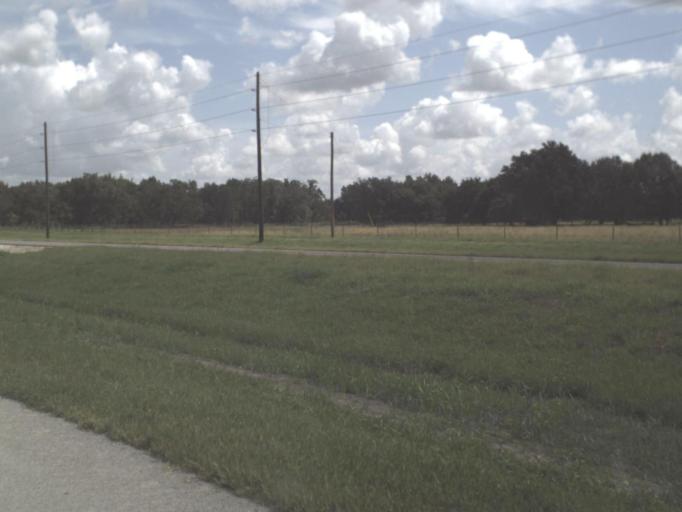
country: US
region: Florida
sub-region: DeSoto County
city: Nocatee
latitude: 27.1467
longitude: -81.8926
